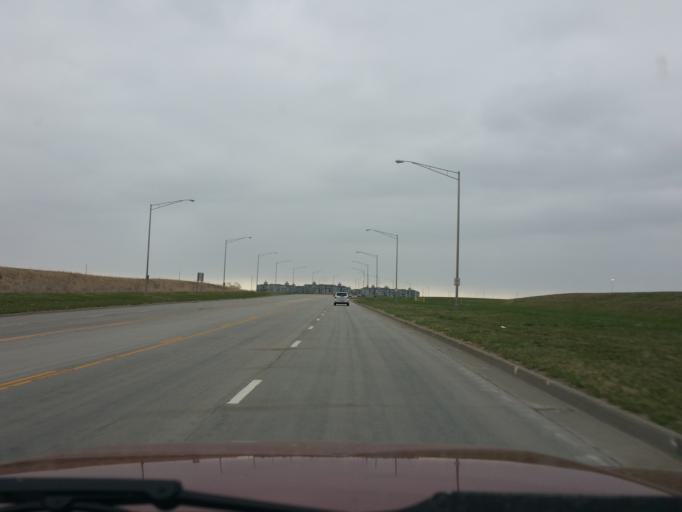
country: US
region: Kansas
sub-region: Wyandotte County
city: Edwardsville
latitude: 39.1187
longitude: -94.8461
